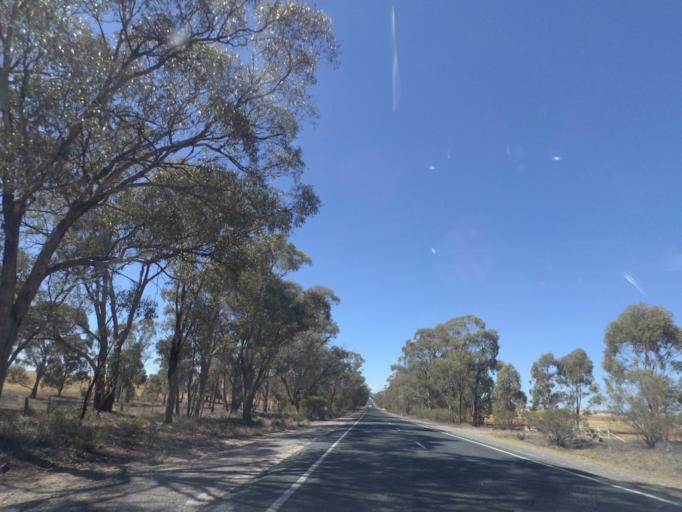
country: AU
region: New South Wales
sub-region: Bland
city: West Wyalong
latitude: -34.1471
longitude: 147.1191
